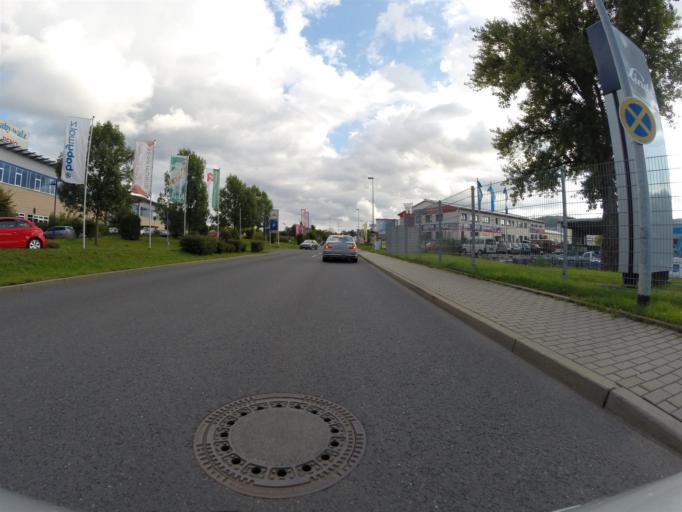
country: DE
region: Thuringia
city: Jena
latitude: 50.9002
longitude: 11.5927
